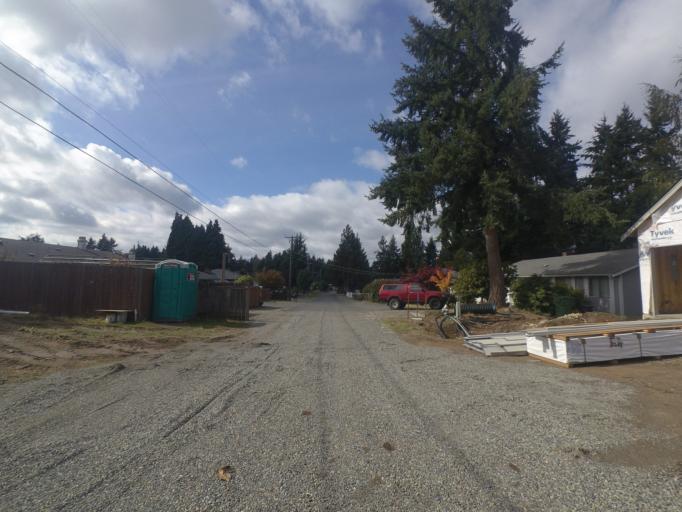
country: US
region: Washington
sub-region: Pierce County
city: University Place
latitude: 47.2231
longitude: -122.5431
